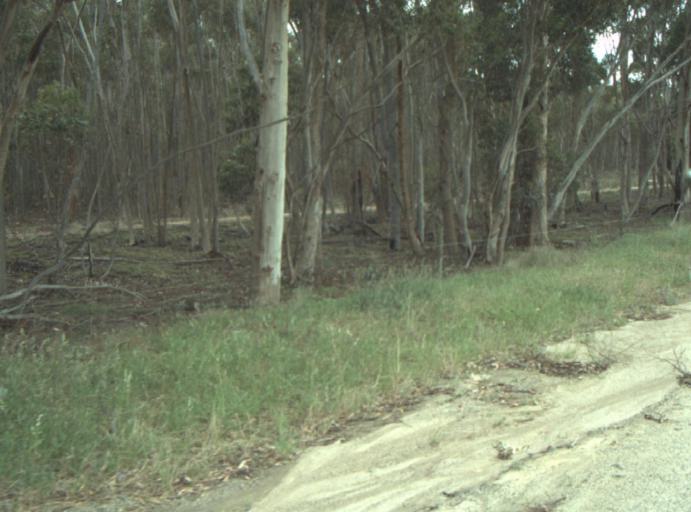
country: AU
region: Victoria
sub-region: Greater Geelong
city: Lara
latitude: -37.9683
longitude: 144.4319
